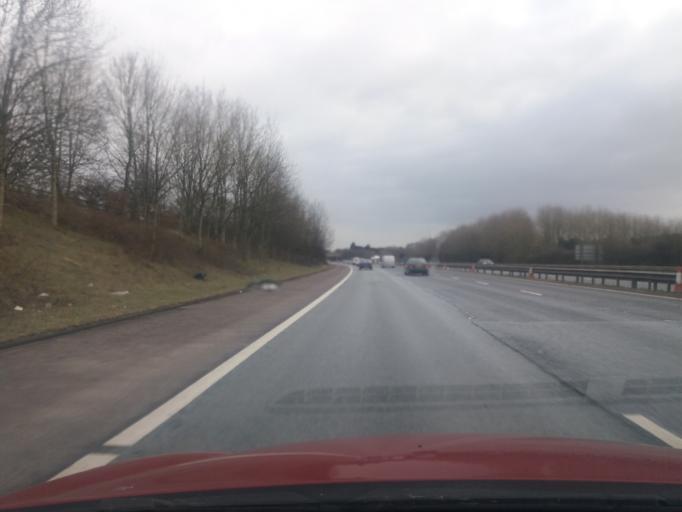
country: GB
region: England
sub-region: Lancashire
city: Chorley
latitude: 53.6804
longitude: -2.6275
